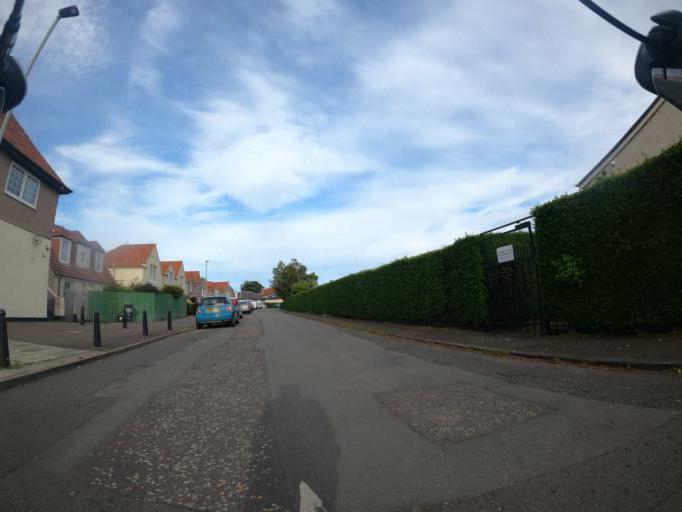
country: GB
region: Scotland
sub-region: Edinburgh
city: Edinburgh
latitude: 55.9746
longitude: -3.2179
